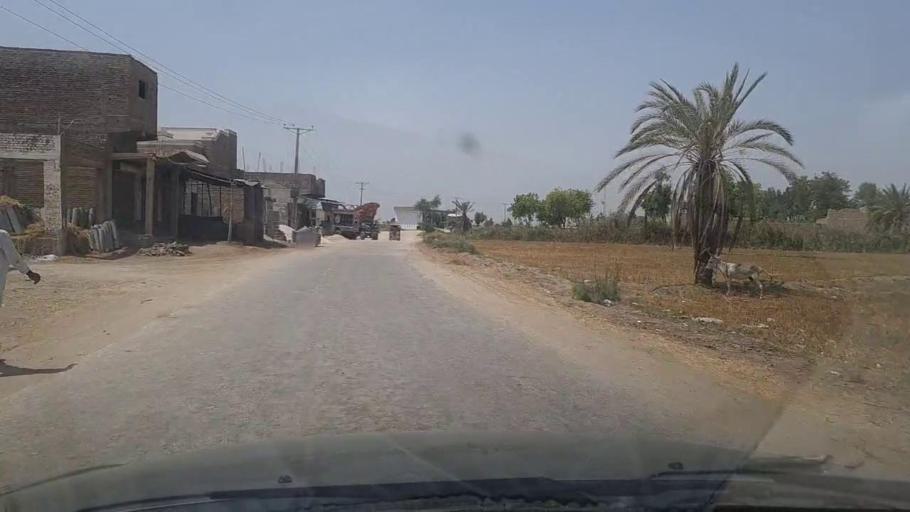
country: PK
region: Sindh
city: Bhiria
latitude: 26.8864
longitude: 68.2685
